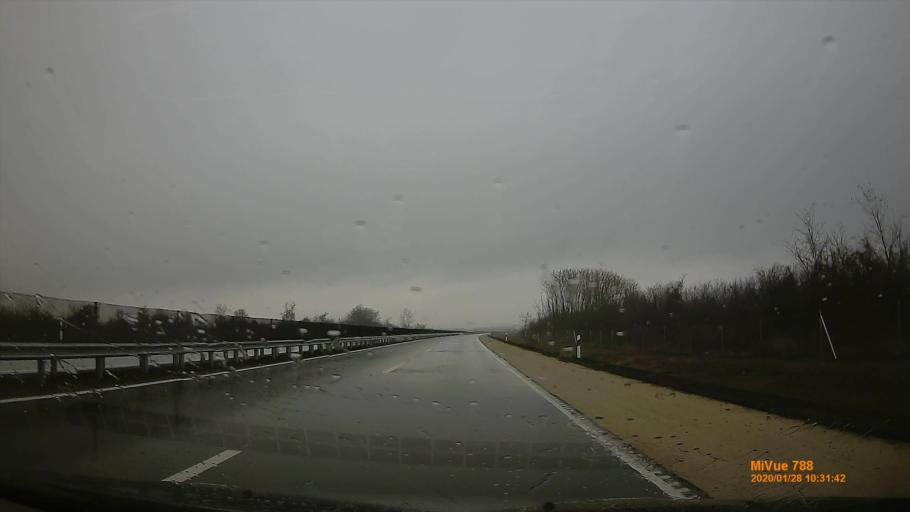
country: HU
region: Pest
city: Gomba
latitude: 47.3419
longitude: 19.5003
